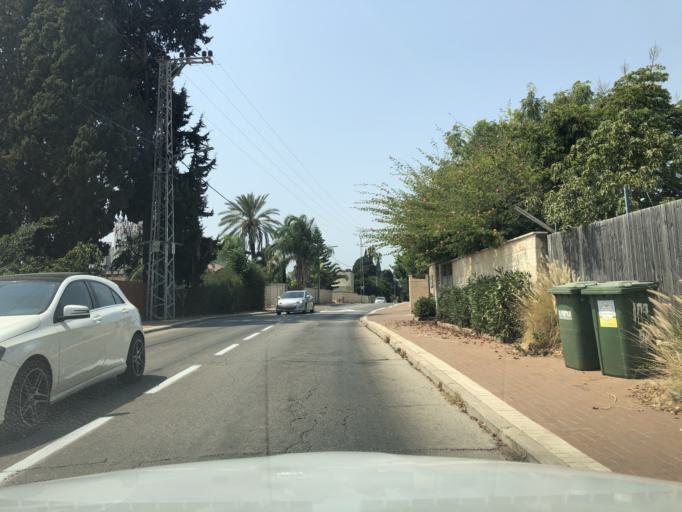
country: IL
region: Central District
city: Ganne Tiqwa
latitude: 32.0685
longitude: 34.8793
